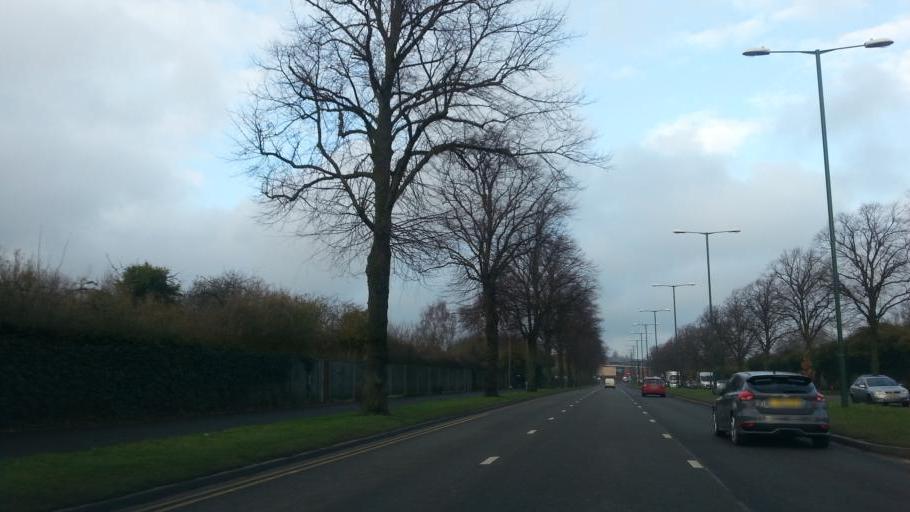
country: GB
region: England
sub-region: Nottingham
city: Nottingham
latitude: 52.9641
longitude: -1.1909
